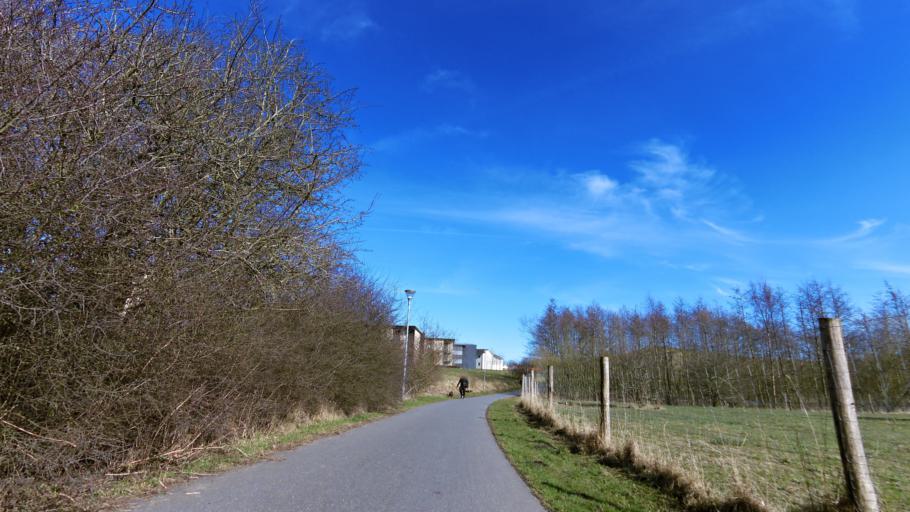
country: DK
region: Central Jutland
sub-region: Arhus Kommune
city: Stavtrup
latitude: 56.1703
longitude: 10.1342
